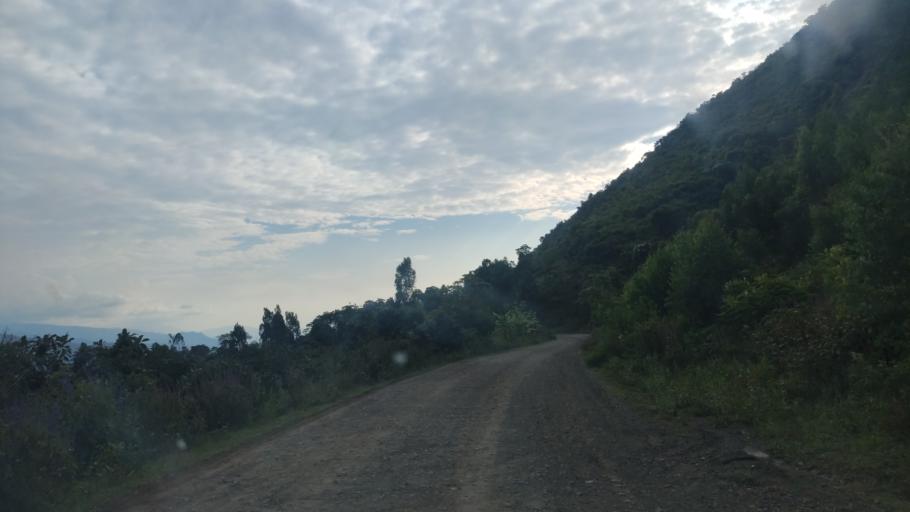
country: ET
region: Southern Nations, Nationalities, and People's Region
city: Arba Minch'
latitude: 6.4432
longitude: 37.3932
